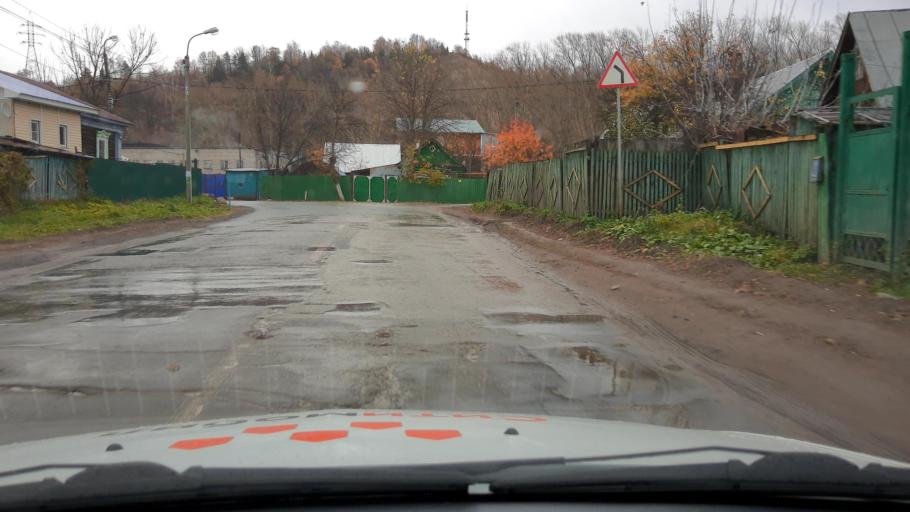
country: RU
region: Bashkortostan
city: Ufa
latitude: 54.7260
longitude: 55.9094
